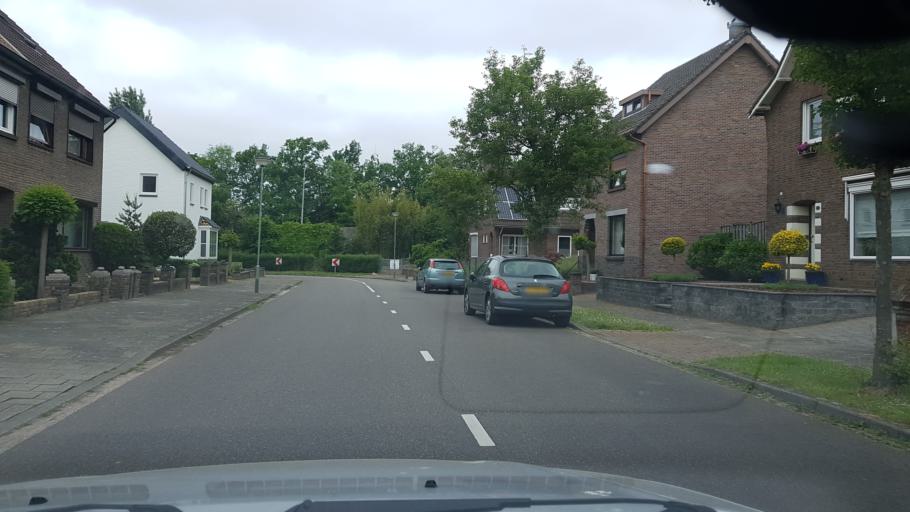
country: NL
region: Limburg
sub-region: Gemeente Stein
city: Stein
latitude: 50.9620
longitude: 5.7662
